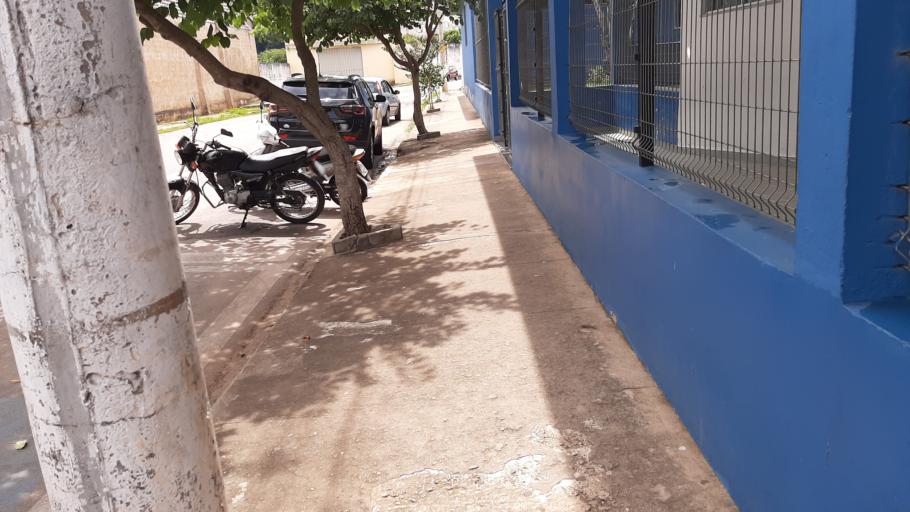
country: BR
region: Minas Gerais
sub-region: Lavras
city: Lavras
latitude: -21.2274
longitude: -45.0039
